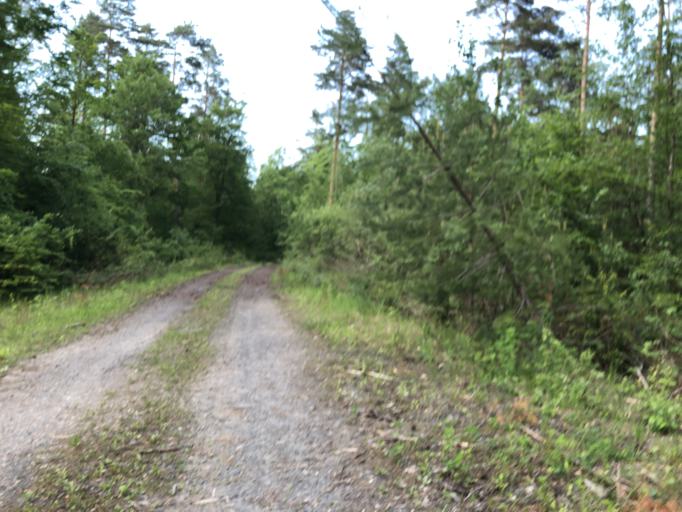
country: DE
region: Bavaria
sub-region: Upper Franconia
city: Memmelsdorf
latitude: 49.9085
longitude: 10.9534
